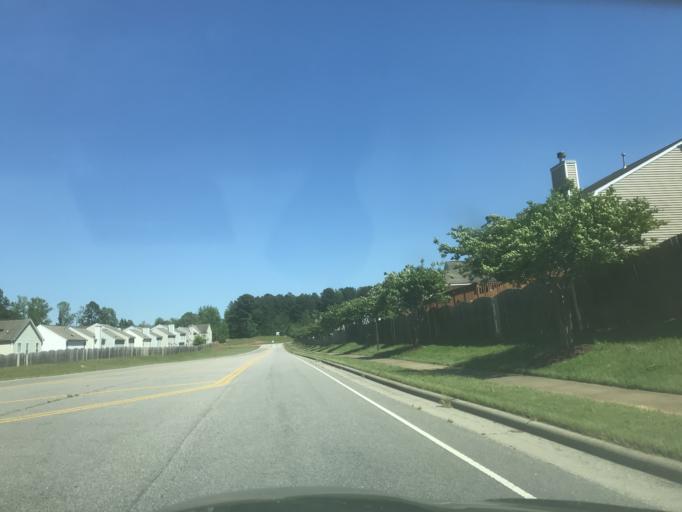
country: US
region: North Carolina
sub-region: Wake County
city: Garner
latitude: 35.7315
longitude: -78.6248
